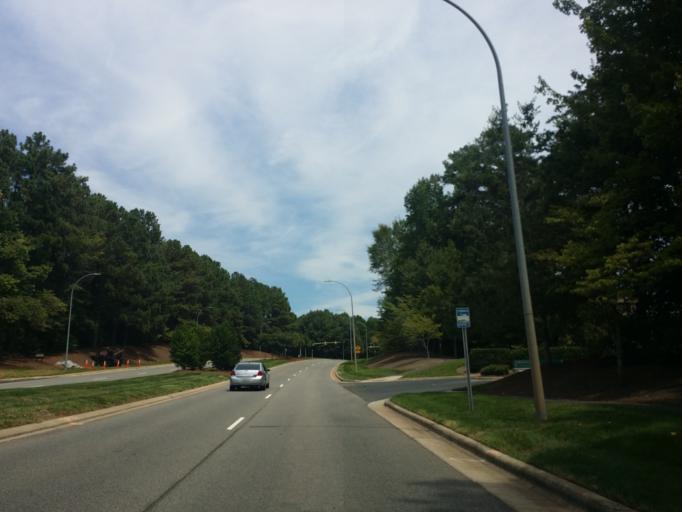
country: US
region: North Carolina
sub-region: Wake County
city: Cary
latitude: 35.8306
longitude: -78.7847
